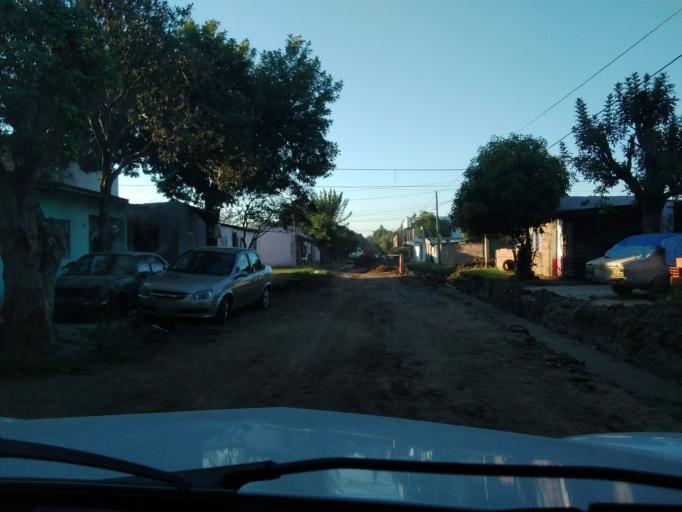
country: AR
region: Corrientes
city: Corrientes
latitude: -27.4789
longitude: -58.7872
